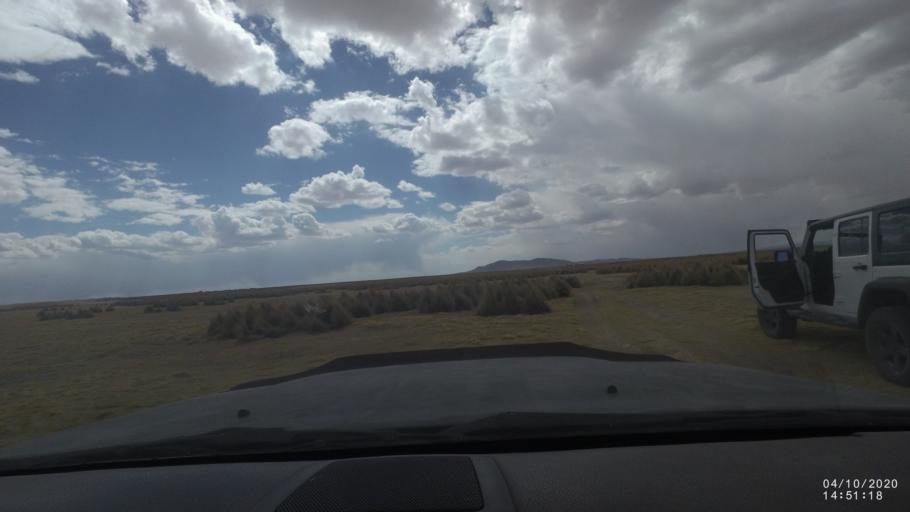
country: BO
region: Oruro
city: Poopo
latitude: -18.6866
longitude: -67.5096
